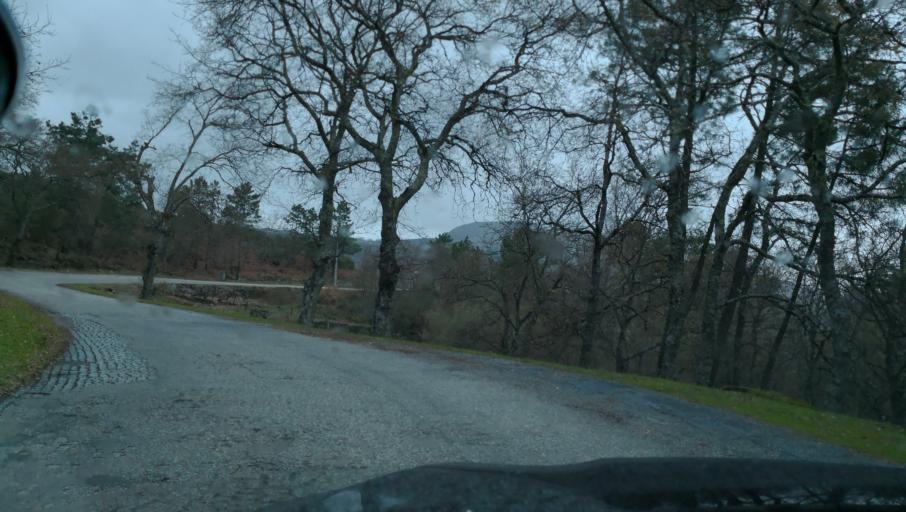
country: PT
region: Vila Real
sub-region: Vila Real
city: Vila Real
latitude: 41.2805
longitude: -7.7969
